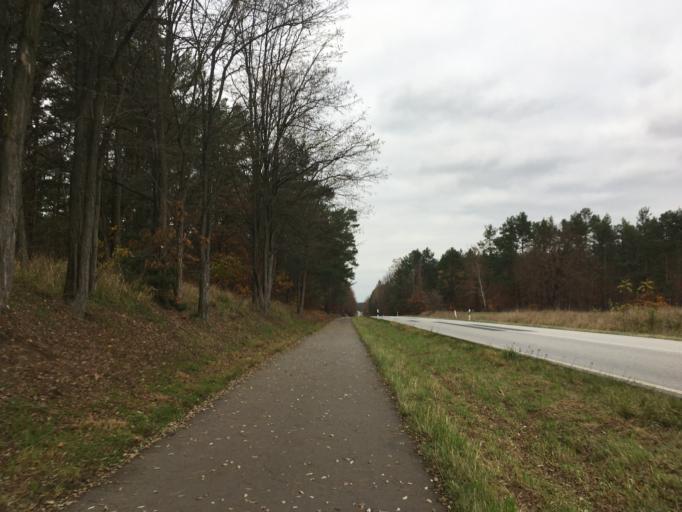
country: DE
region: Brandenburg
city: Mixdorf
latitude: 52.2021
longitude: 14.4570
